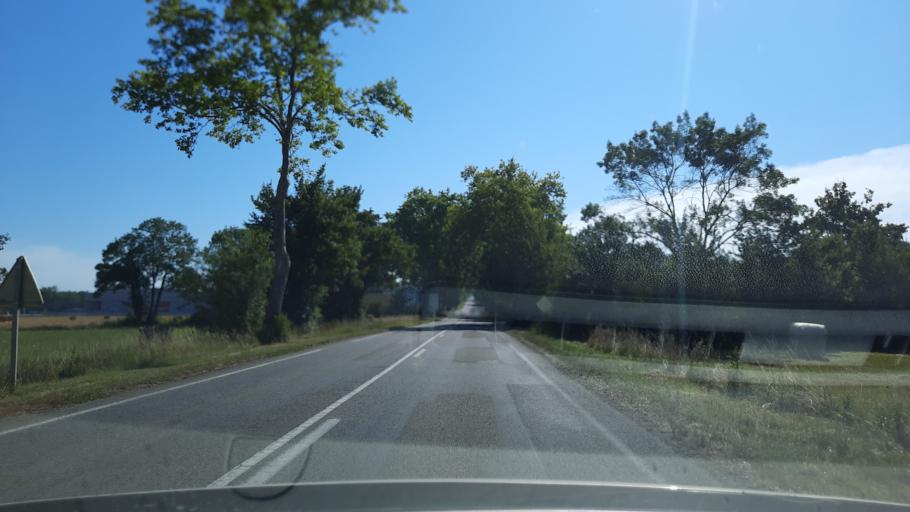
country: FR
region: Midi-Pyrenees
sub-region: Departement du Tarn-et-Garonne
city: Monteils
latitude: 44.1657
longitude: 1.5637
